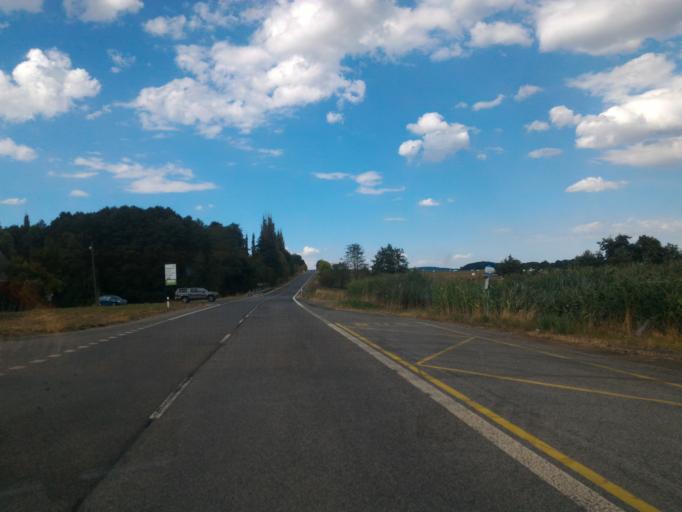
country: CZ
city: Jablonne v Podjestedi
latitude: 50.7352
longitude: 14.7582
